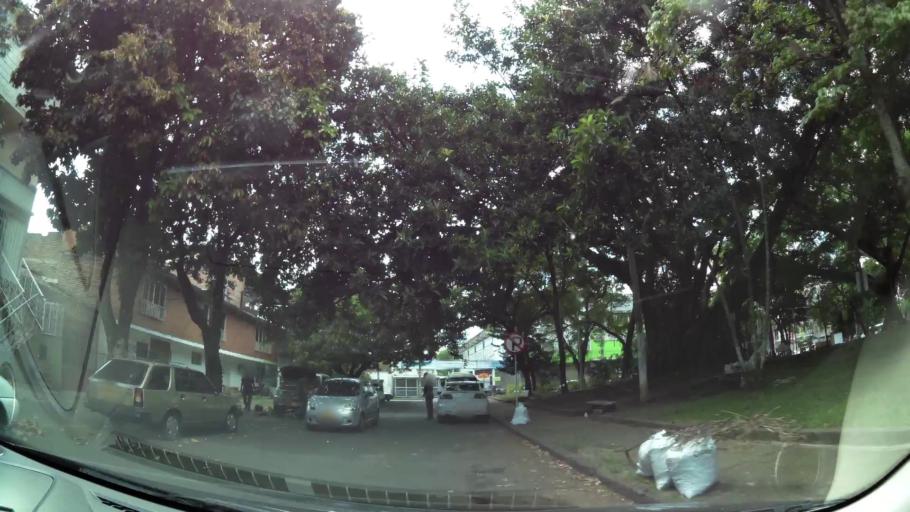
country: CO
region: Valle del Cauca
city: Cali
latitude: 3.4057
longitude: -76.5457
